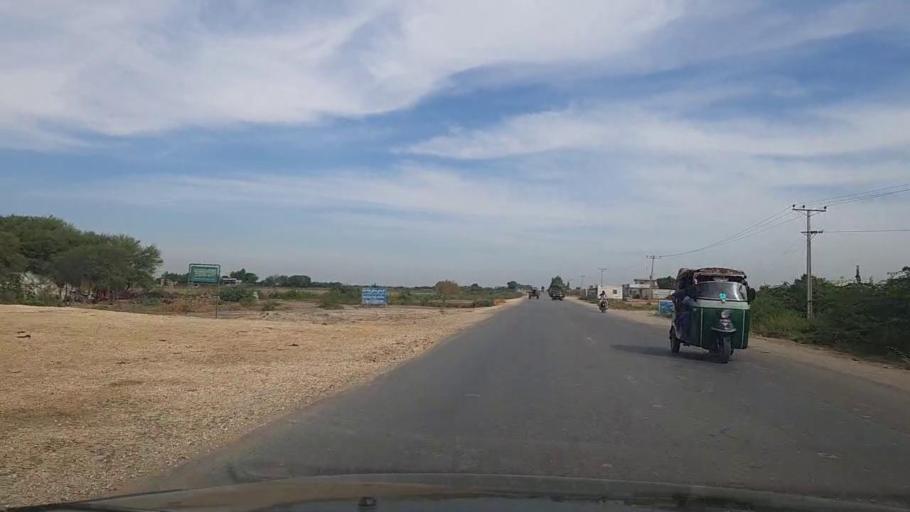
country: PK
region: Sindh
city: Thatta
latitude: 24.7613
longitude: 67.9330
